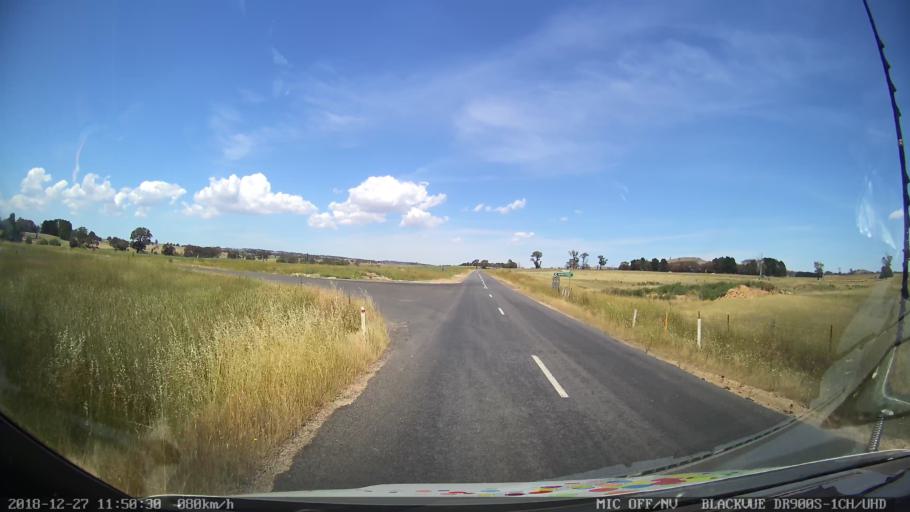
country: AU
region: New South Wales
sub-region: Bathurst Regional
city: Perthville
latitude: -33.6329
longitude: 149.4301
